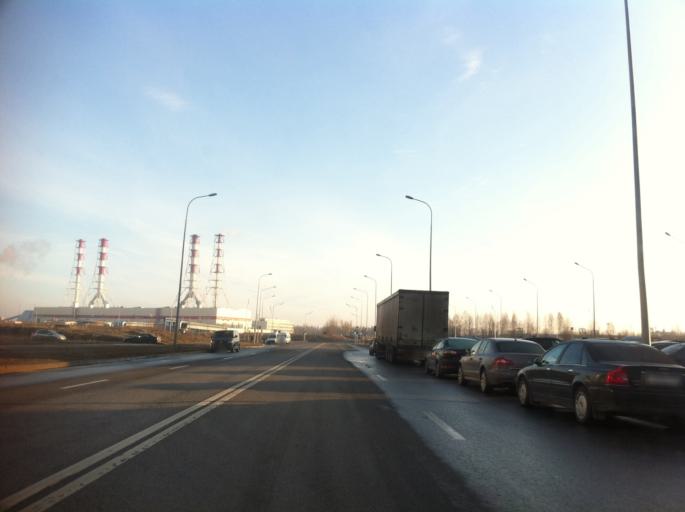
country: RU
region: St.-Petersburg
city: Uritsk
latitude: 59.8635
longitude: 30.1815
